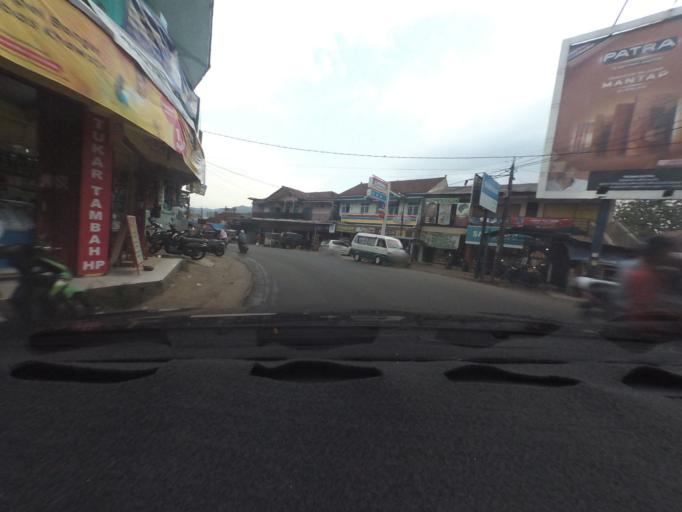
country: ID
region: West Java
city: Gunungkalong
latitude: -6.9540
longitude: 106.7674
